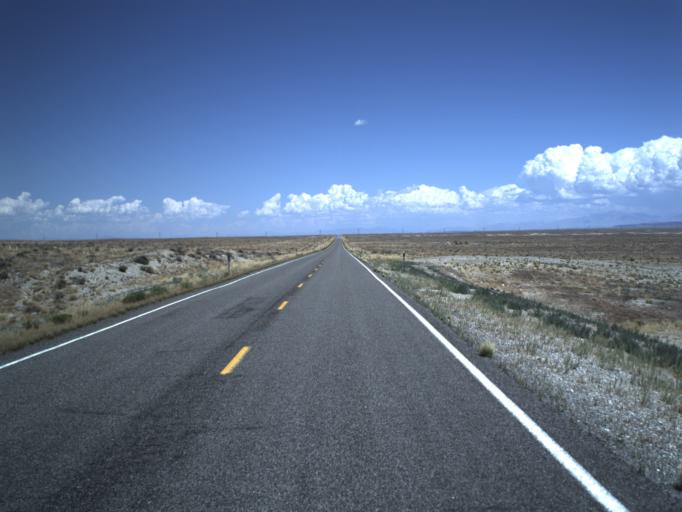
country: US
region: Utah
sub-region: Millard County
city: Delta
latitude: 39.1526
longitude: -113.0651
